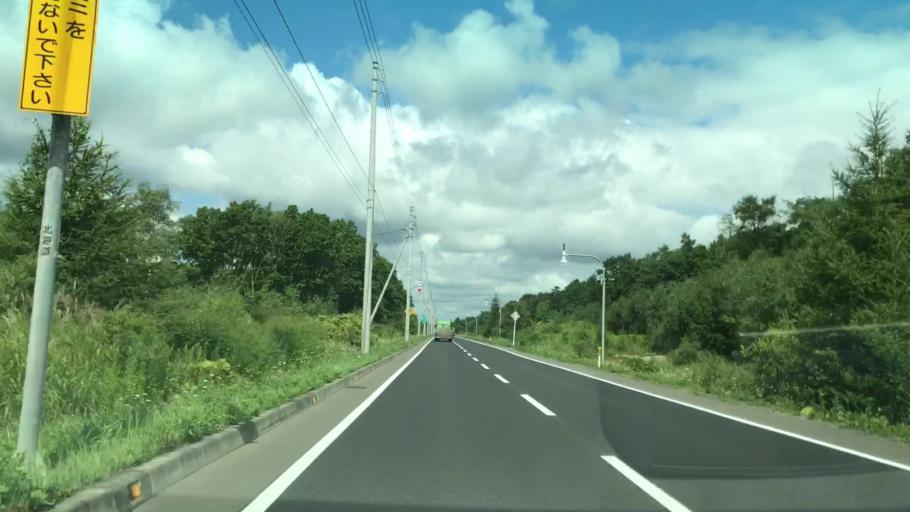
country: JP
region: Hokkaido
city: Chitose
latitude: 42.7655
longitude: 141.6637
